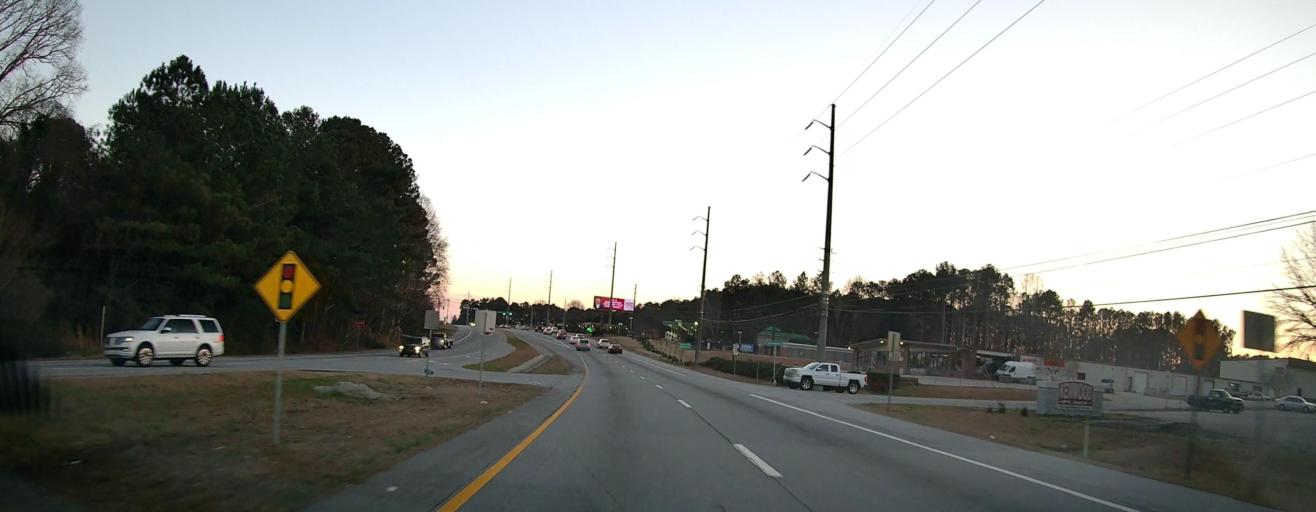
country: US
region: Georgia
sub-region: Clayton County
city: Riverdale
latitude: 33.5122
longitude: -84.4299
